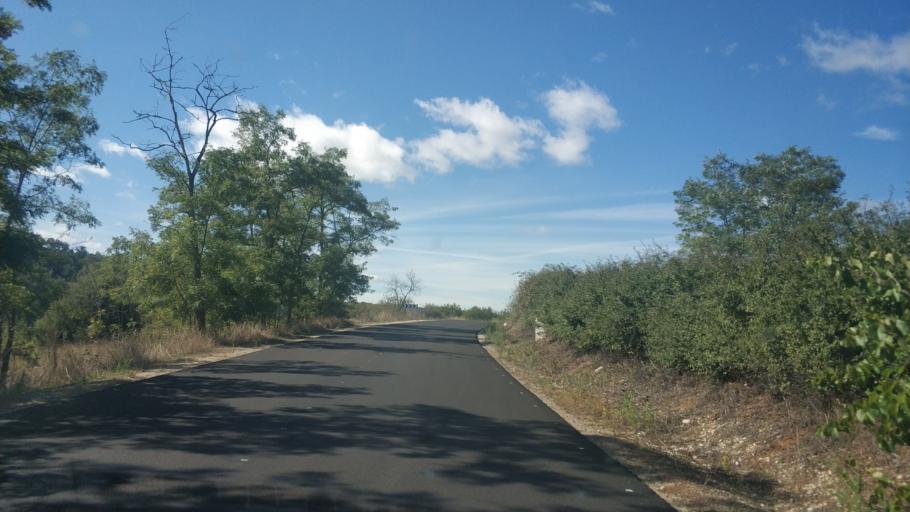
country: ES
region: Castille and Leon
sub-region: Provincia de Burgos
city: Covarrubias
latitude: 42.0492
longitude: -3.5244
